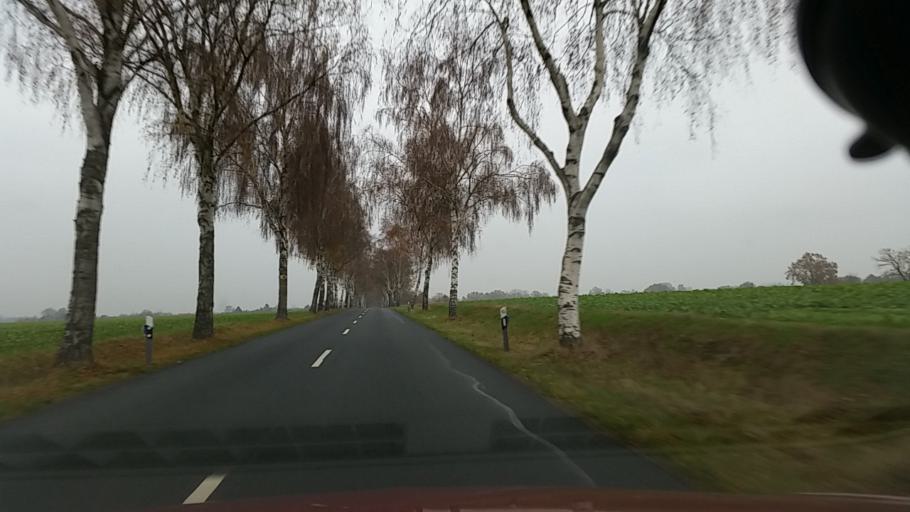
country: DE
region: Lower Saxony
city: Stadensen
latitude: 52.8720
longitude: 10.5795
